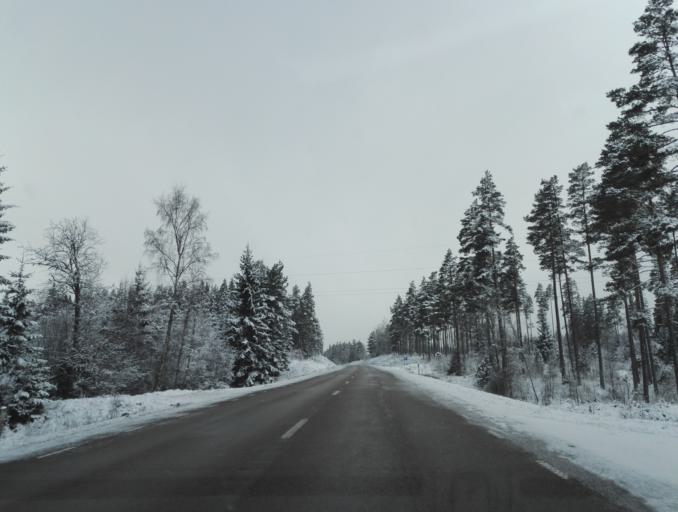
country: SE
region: Kronoberg
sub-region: Uppvidinge Kommun
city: Aseda
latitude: 57.1346
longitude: 15.2780
